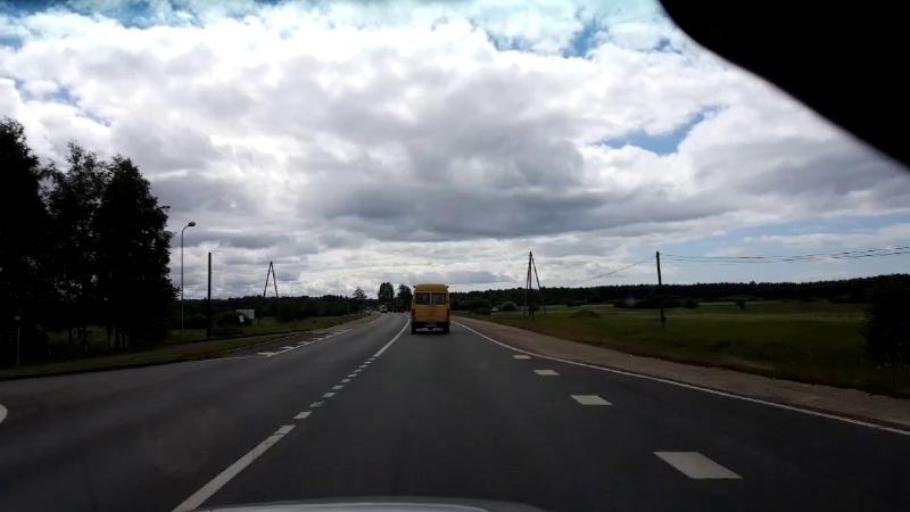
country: LV
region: Salacgrivas
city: Salacgriva
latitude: 57.7395
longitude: 24.3626
